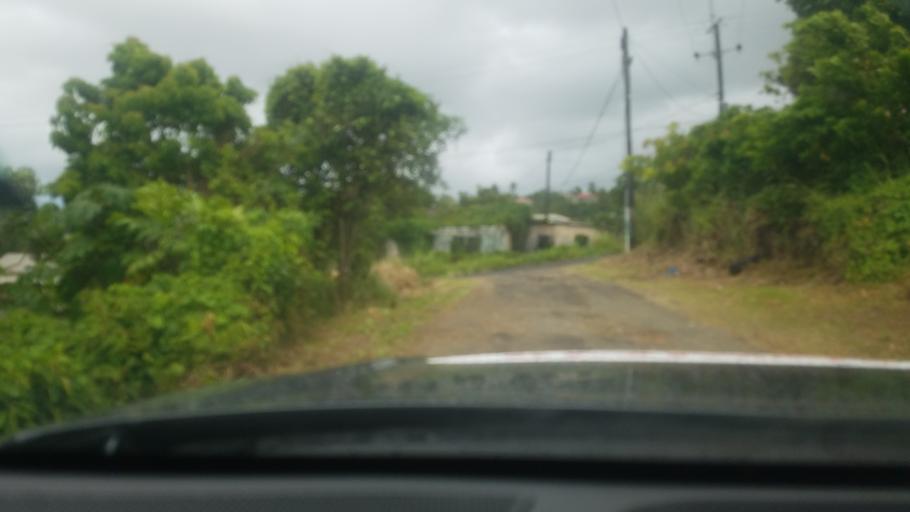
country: LC
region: Micoud Quarter
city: Micoud
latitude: 13.8075
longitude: -60.9467
